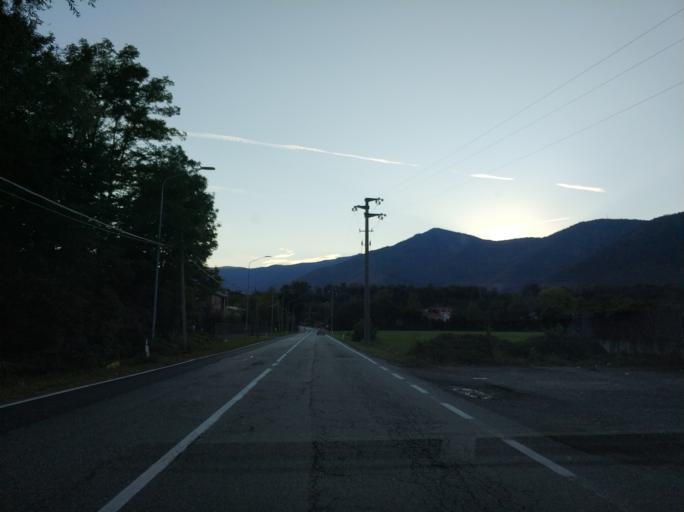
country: IT
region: Piedmont
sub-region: Provincia di Torino
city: Cafasse
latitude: 45.2380
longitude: 7.5299
